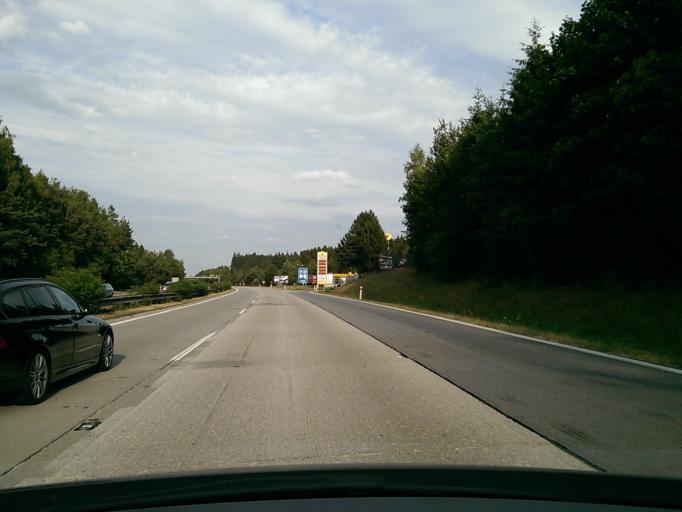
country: CZ
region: Vysocina
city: Luka nad Jihlavou
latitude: 49.4127
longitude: 15.7173
